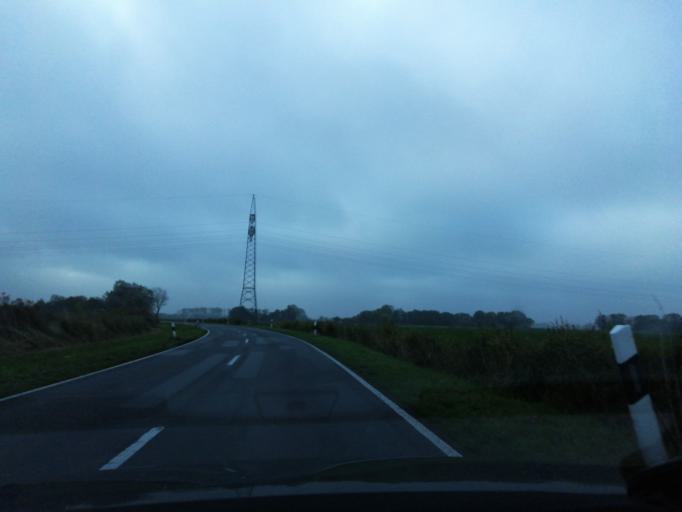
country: DE
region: Lower Saxony
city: Jever
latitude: 53.6695
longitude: 7.8630
